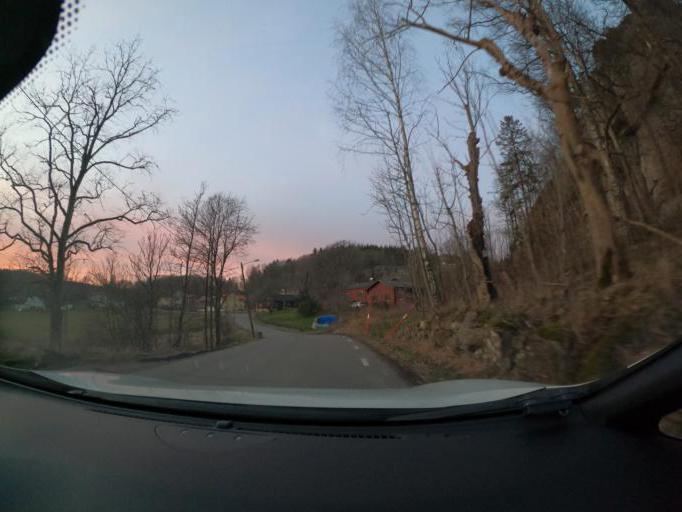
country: SE
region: Vaestra Goetaland
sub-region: Harryda Kommun
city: Molnlycke
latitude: 57.6069
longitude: 12.1556
